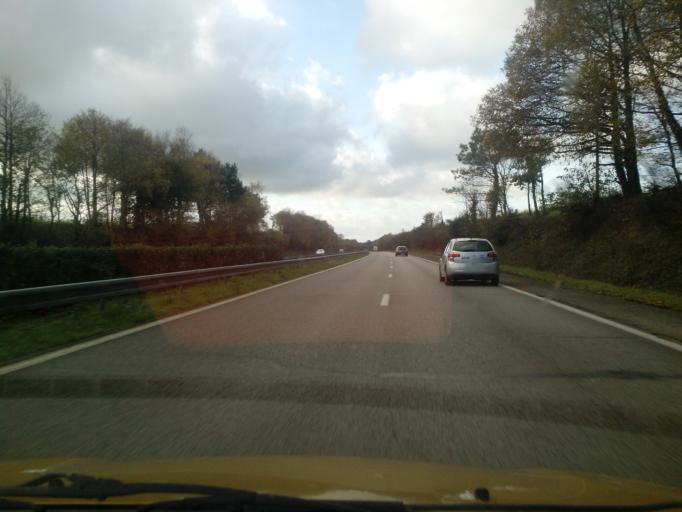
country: FR
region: Brittany
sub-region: Departement du Morbihan
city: Branderion
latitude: 47.8118
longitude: -3.2268
